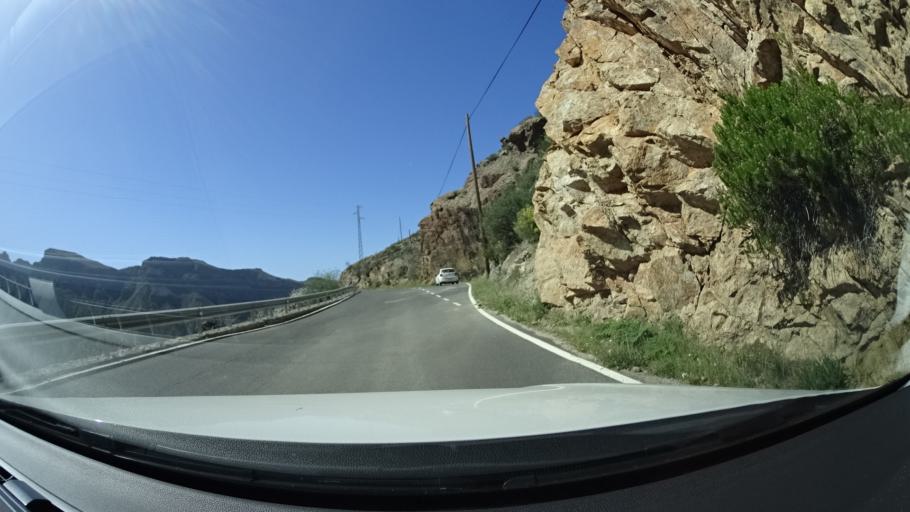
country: ES
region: Canary Islands
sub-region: Provincia de Las Palmas
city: Tejeda
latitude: 27.9889
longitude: -15.6355
